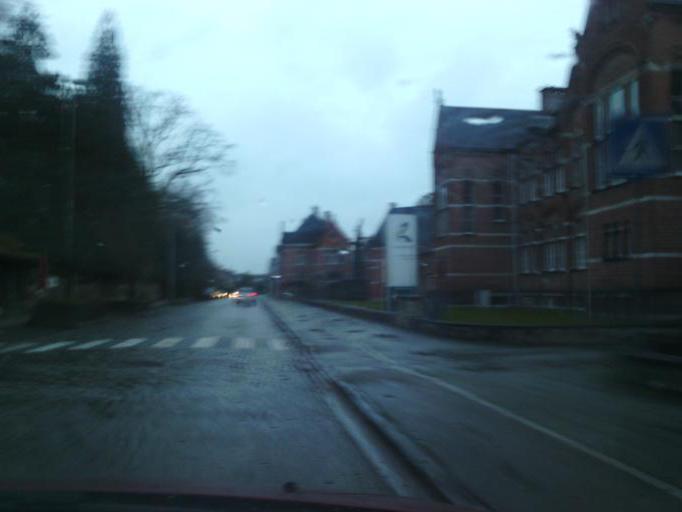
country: BE
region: Flanders
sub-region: Provincie Oost-Vlaanderen
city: Lokeren
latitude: 51.1071
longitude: 3.9848
